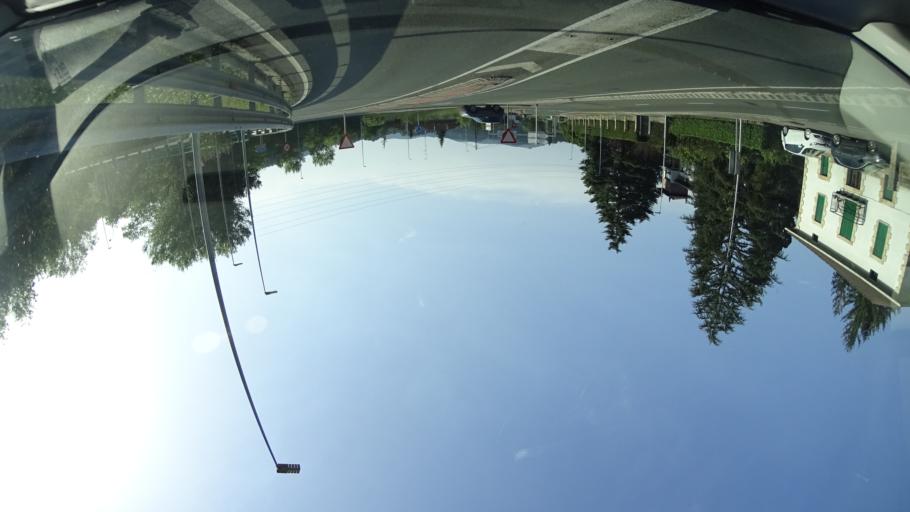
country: ES
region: Basque Country
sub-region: Bizkaia
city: Galdakao
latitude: 43.2270
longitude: -2.8196
